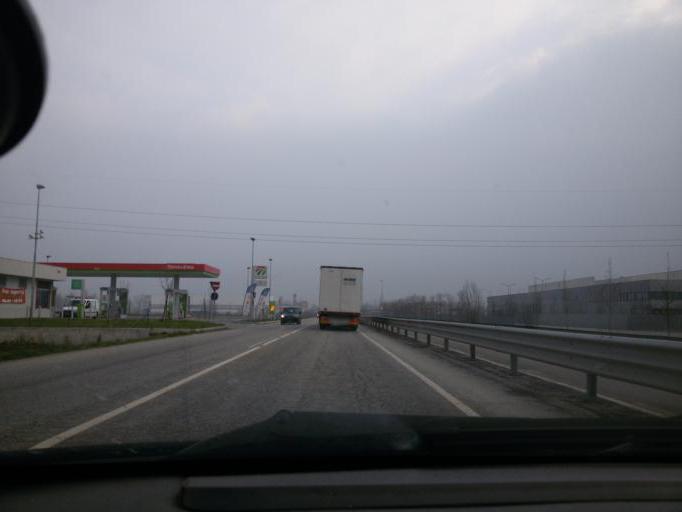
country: IT
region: Piedmont
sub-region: Provincia di Vercelli
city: Vercelli
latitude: 45.2997
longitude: 8.3917
